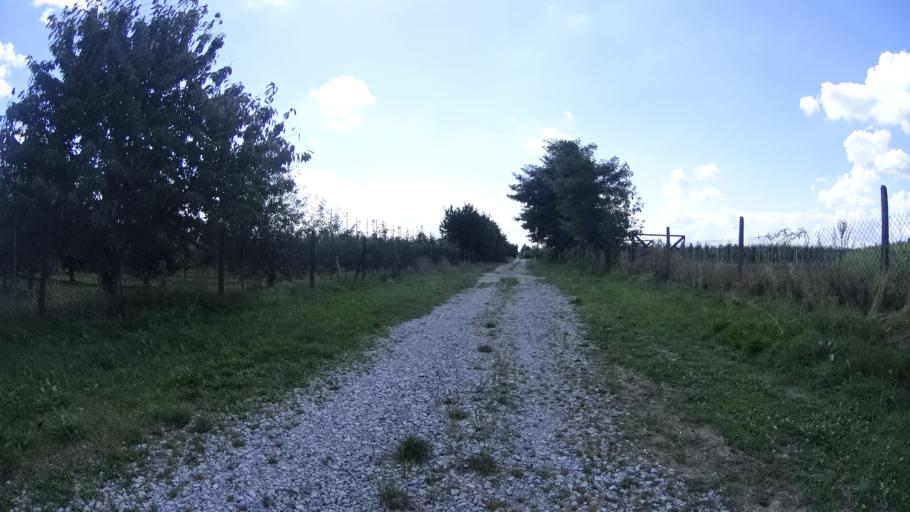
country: PL
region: Masovian Voivodeship
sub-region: Powiat grojecki
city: Mogielnica
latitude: 51.6854
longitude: 20.7691
